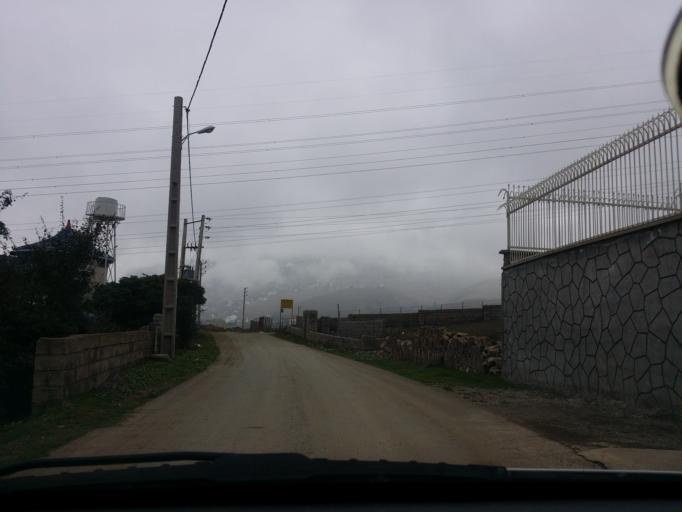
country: IR
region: Mazandaran
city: Chalus
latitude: 36.5127
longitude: 51.2295
